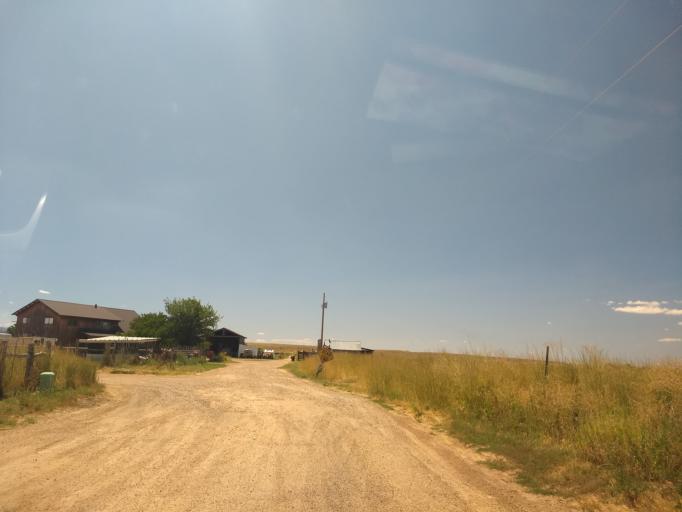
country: US
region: Arizona
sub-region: Coconino County
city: Fredonia
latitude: 36.9296
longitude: -112.5353
